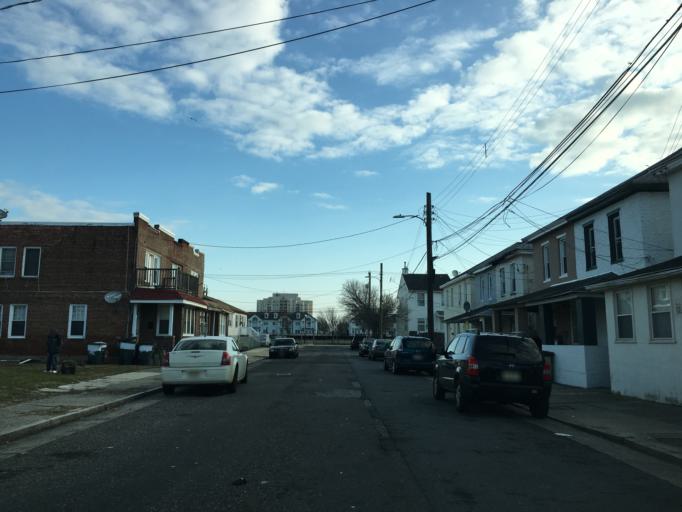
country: US
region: New Jersey
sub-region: Atlantic County
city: Atlantic City
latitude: 39.3711
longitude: -74.4209
